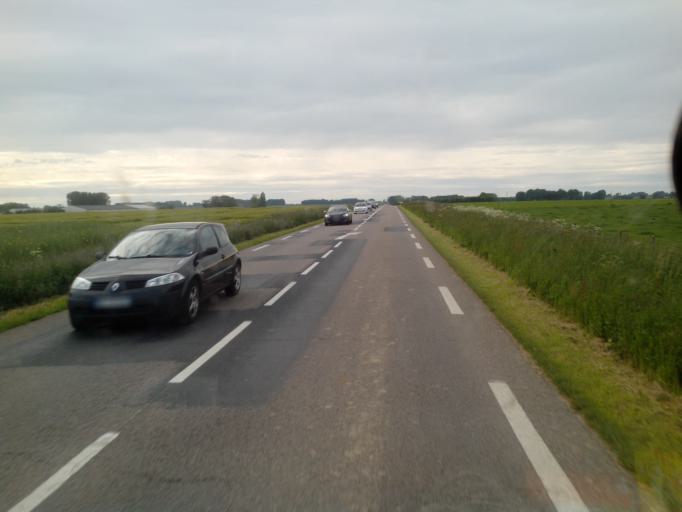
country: FR
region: Haute-Normandie
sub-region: Departement de la Seine-Maritime
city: Fauville-en-Caux
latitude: 49.6700
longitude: 0.5755
